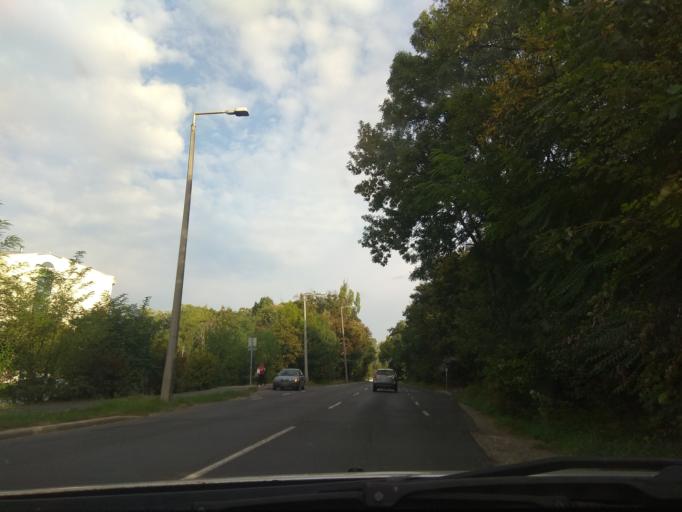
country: HU
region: Borsod-Abauj-Zemplen
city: Miskolc
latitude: 48.0788
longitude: 20.7721
